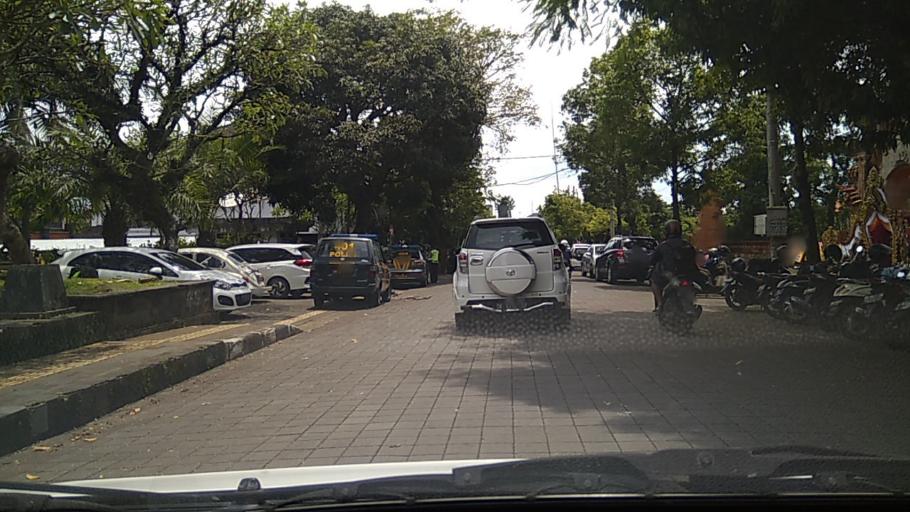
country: ID
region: Bali
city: Tabanan
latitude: -8.5374
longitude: 115.1260
